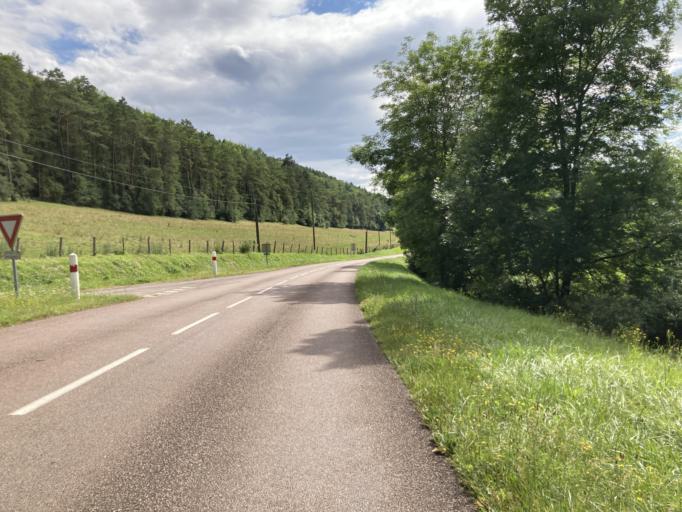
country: FR
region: Bourgogne
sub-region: Departement de la Cote-d'Or
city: Montbard
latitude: 47.6338
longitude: 4.3743
